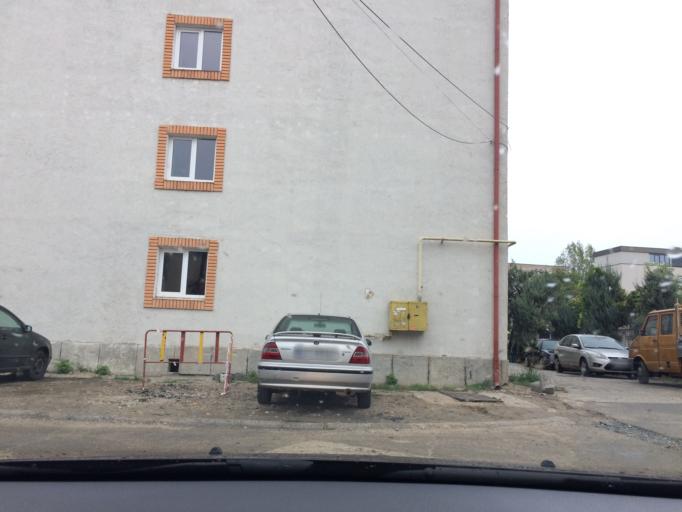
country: RO
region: Timis
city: Timisoara
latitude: 45.7508
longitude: 21.2438
